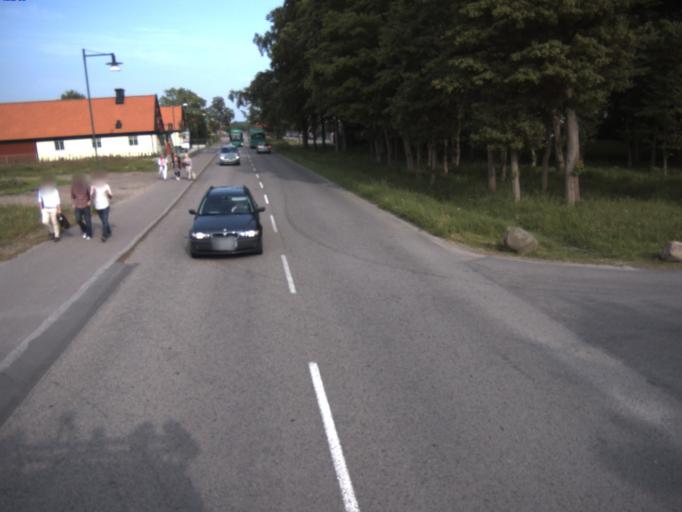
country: SE
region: Skane
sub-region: Helsingborg
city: Helsingborg
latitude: 56.0825
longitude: 12.6888
